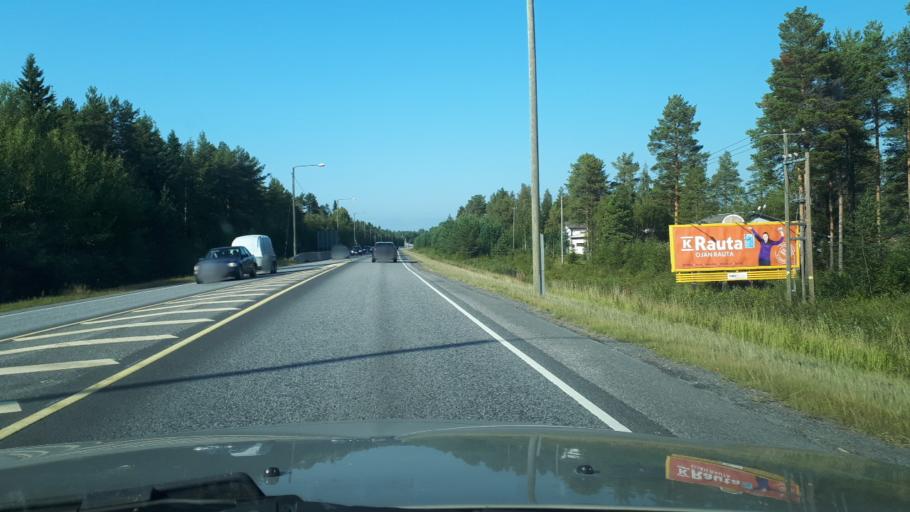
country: FI
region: Northern Ostrobothnia
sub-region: Oulunkaari
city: Ii
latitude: 65.3102
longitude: 25.3741
